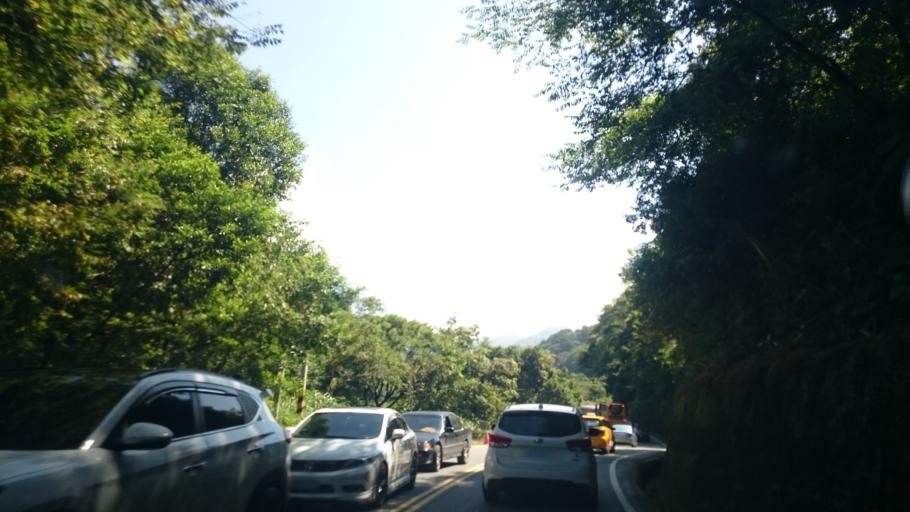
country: TW
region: Taiwan
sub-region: Nantou
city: Puli
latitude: 24.0091
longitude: 121.1147
